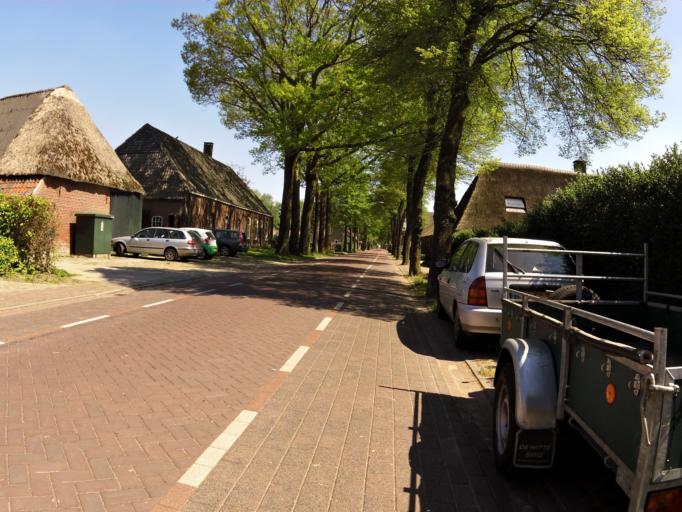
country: NL
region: North Brabant
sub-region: Gemeente Haaren
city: Haaren
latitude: 51.6616
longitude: 5.2259
